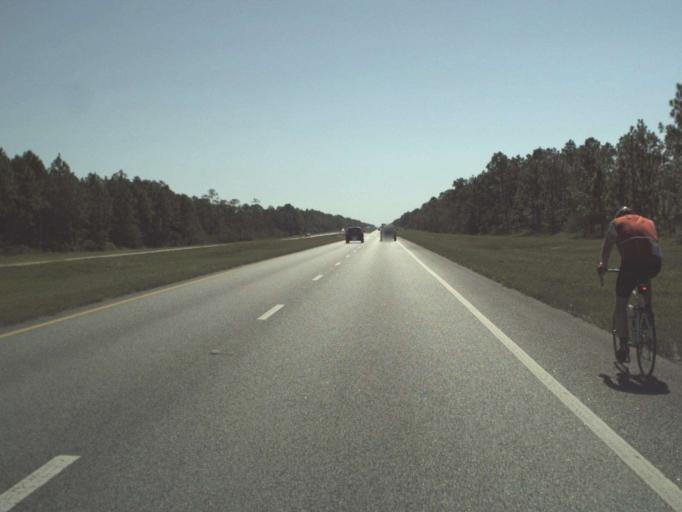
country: US
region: Florida
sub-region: Walton County
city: Seaside
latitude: 30.3242
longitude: -86.0496
